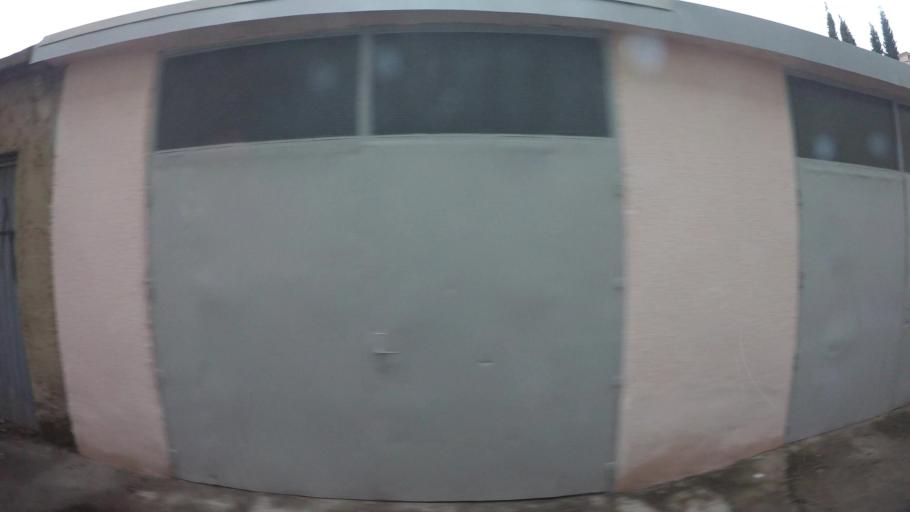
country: BA
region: Federation of Bosnia and Herzegovina
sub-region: Hercegovacko-Bosanski Kanton
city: Mostar
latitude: 43.3409
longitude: 17.8051
